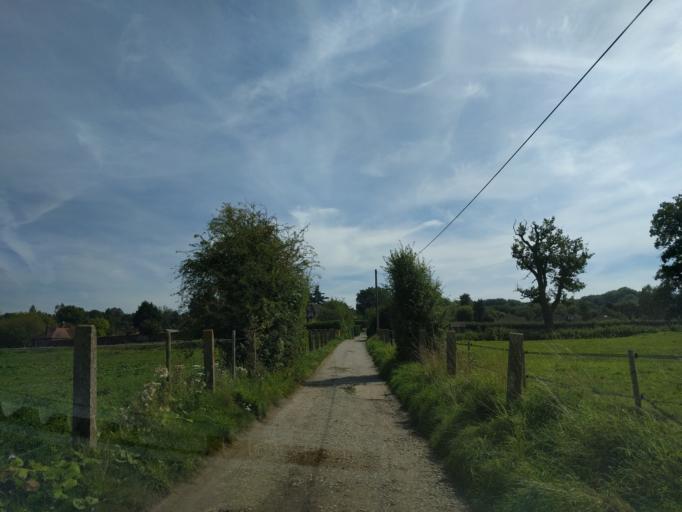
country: GB
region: England
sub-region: Surrey
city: Chilworth
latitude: 51.2177
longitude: -0.5199
